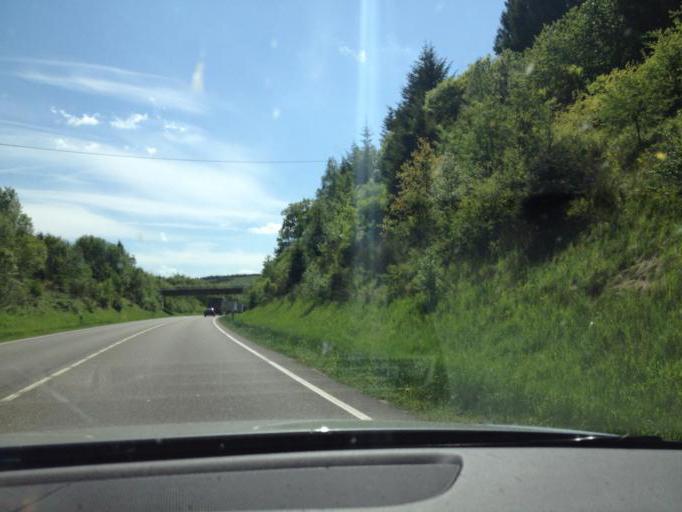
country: DE
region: Rheinland-Pfalz
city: Oberlauch
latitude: 50.1808
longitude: 6.4163
